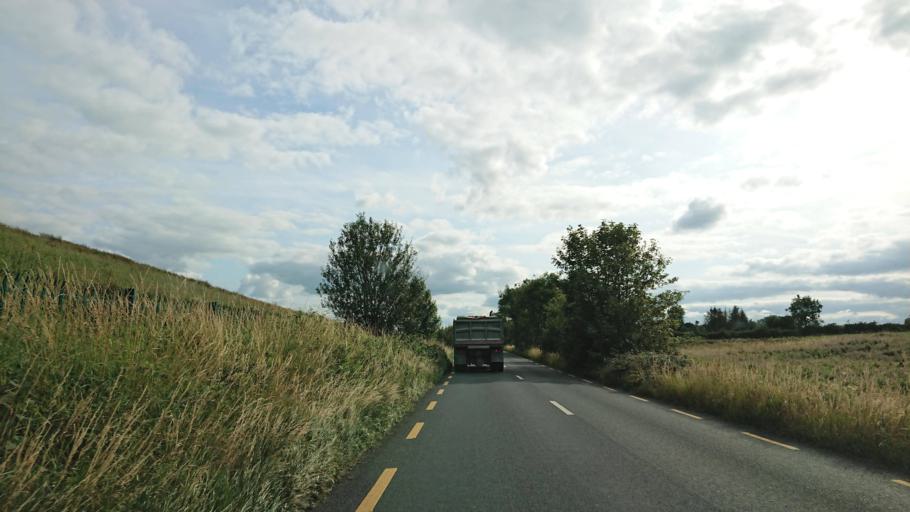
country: IE
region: Connaught
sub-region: County Leitrim
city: Carrick-on-Shannon
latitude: 53.9598
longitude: -8.0788
